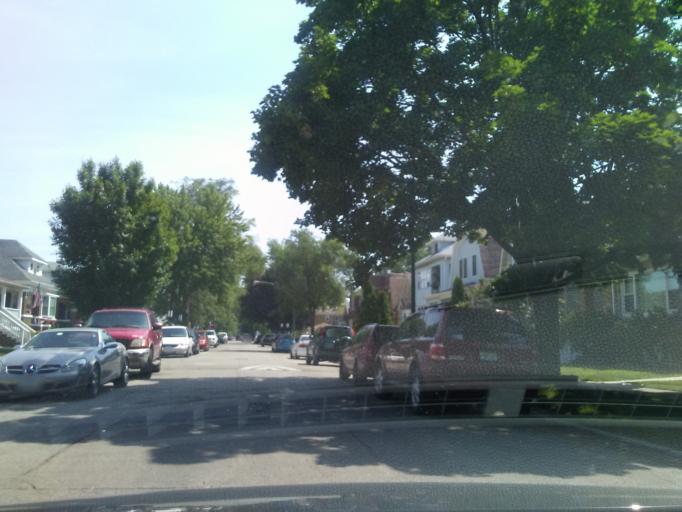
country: US
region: Illinois
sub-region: Cook County
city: Lincolnwood
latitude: 41.9767
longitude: -87.7578
